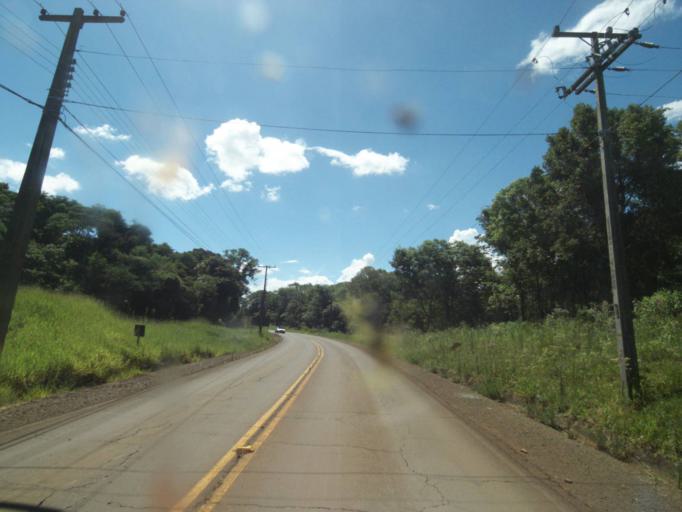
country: BR
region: Parana
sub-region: Chopinzinho
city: Chopinzinho
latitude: -25.7871
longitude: -52.0957
